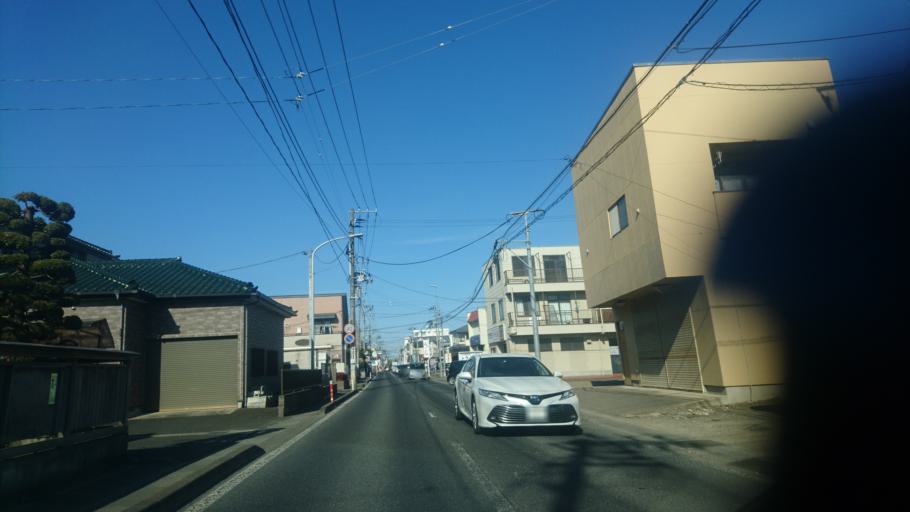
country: JP
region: Miyagi
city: Sendai
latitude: 38.1981
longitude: 140.8851
